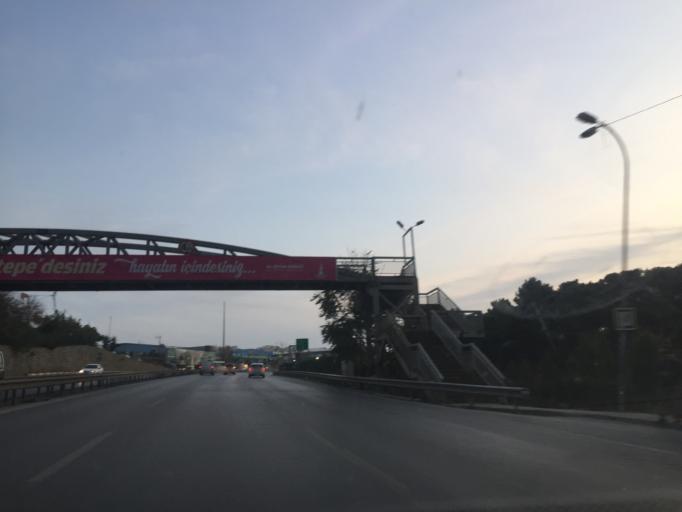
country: TR
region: Istanbul
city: Samandira
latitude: 40.9721
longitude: 29.2195
